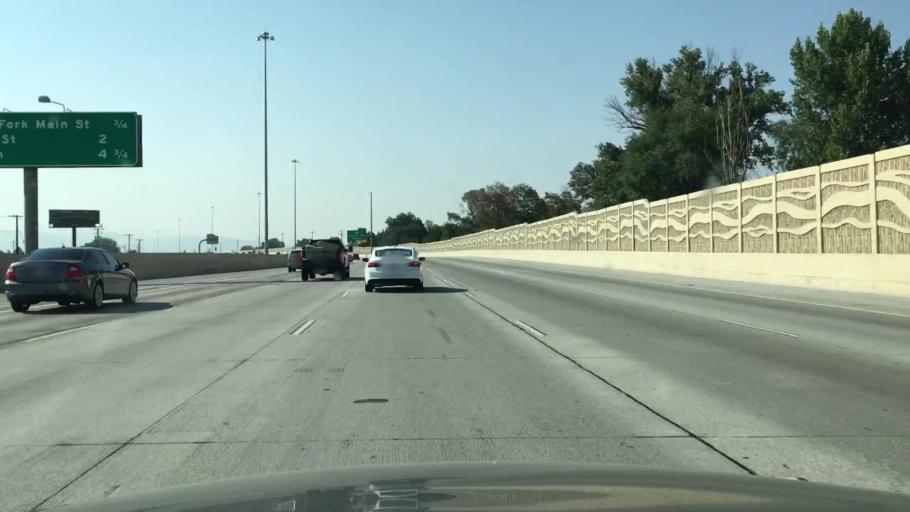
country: US
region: Utah
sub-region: Utah County
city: American Fork
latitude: 40.3705
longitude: -111.7998
